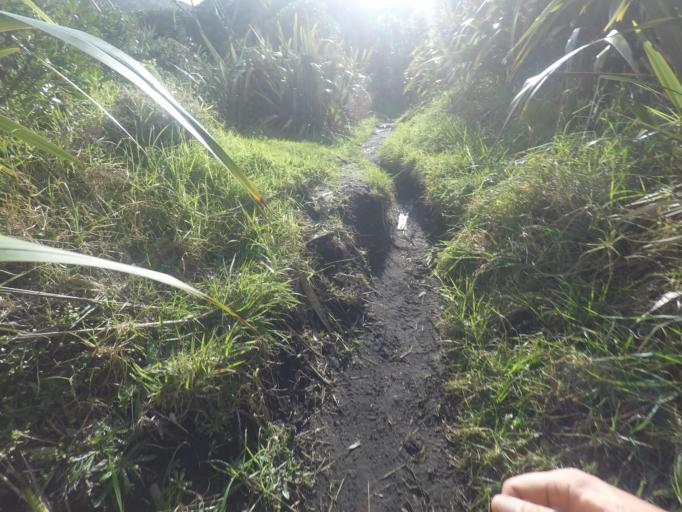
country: NZ
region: Auckland
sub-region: Auckland
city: Muriwai Beach
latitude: -36.8832
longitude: 174.4400
